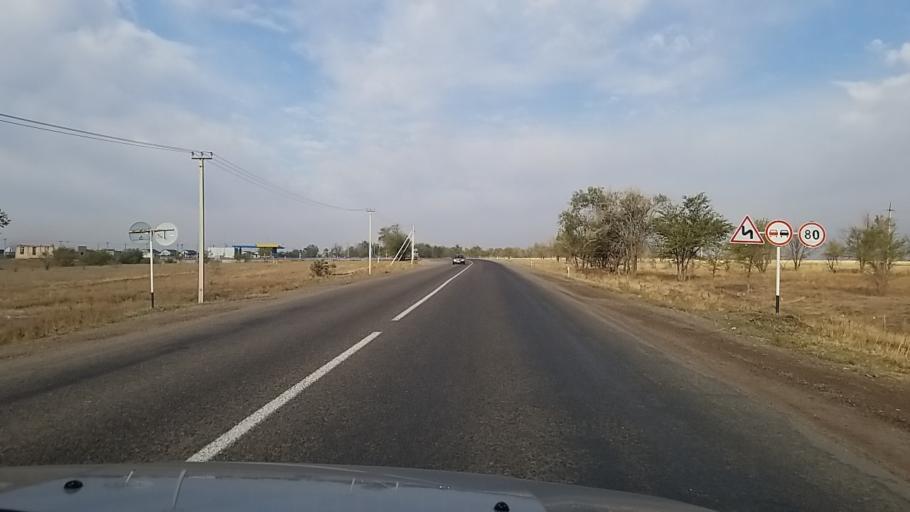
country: KZ
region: Almaty Oblysy
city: Burunday
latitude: 43.4764
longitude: 76.6871
